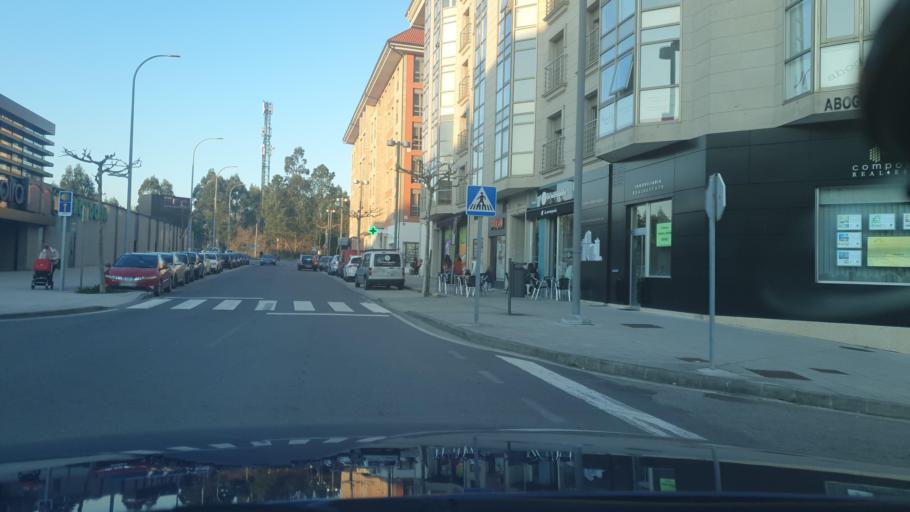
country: ES
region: Galicia
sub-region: Provincia da Coruna
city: Santiago de Compostela
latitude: 42.8474
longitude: -8.5802
